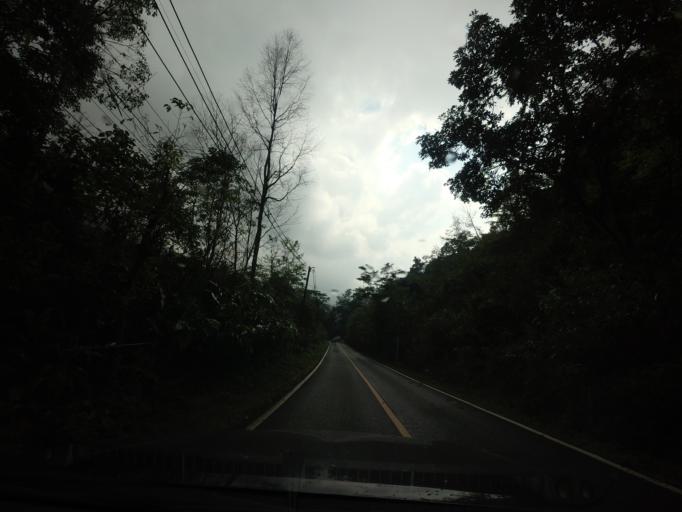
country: TH
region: Nan
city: Bo Kluea
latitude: 19.1945
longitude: 101.0796
